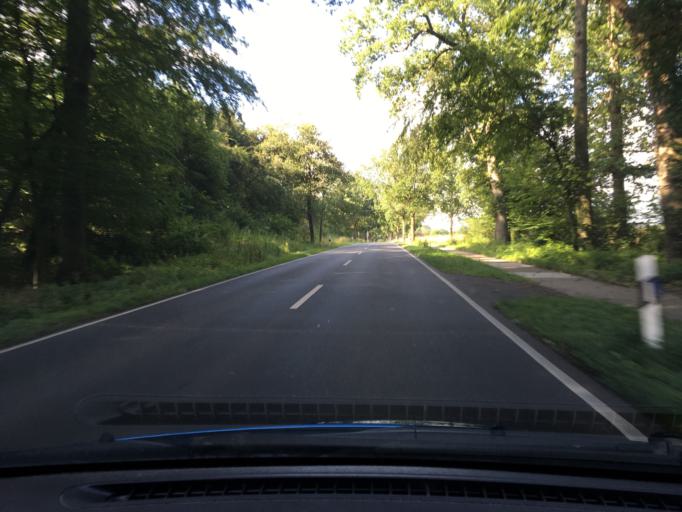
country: DE
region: Lower Saxony
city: Bad Bevensen
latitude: 53.1018
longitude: 10.5974
